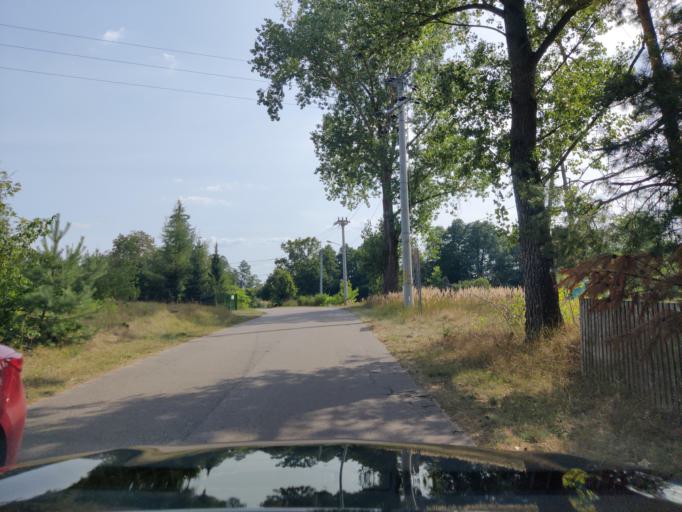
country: PL
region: Masovian Voivodeship
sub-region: Powiat makowski
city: Rozan
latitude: 52.8493
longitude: 21.4571
